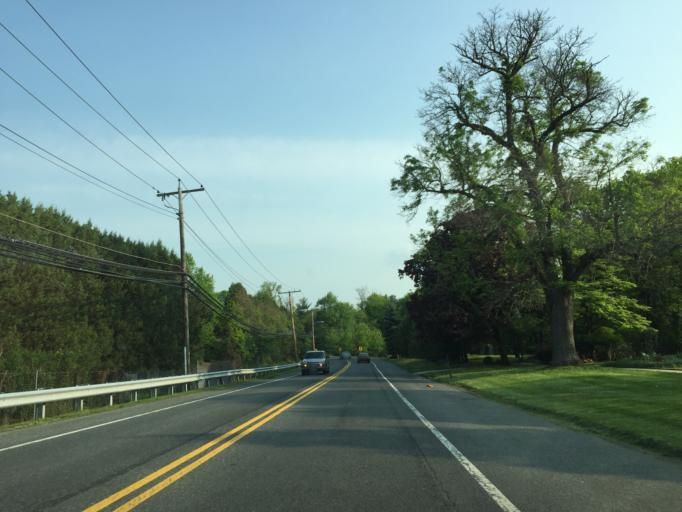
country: US
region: Maryland
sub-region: Baltimore County
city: Pikesville
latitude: 39.3762
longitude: -76.7127
